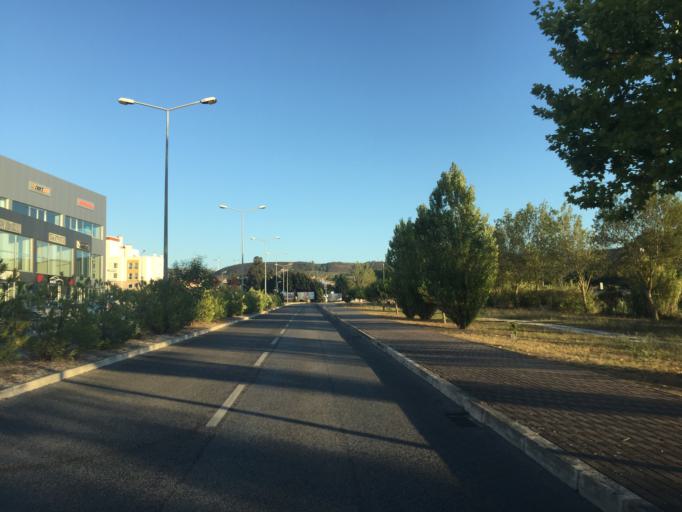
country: PT
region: Lisbon
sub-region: Torres Vedras
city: Torres Vedras
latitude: 39.0770
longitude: -9.2571
